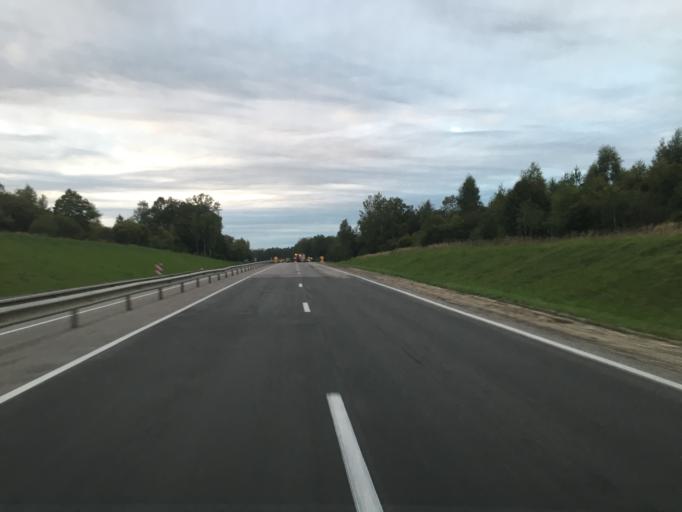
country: RU
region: Kaluga
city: Kaluga
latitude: 54.6051
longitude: 36.3148
